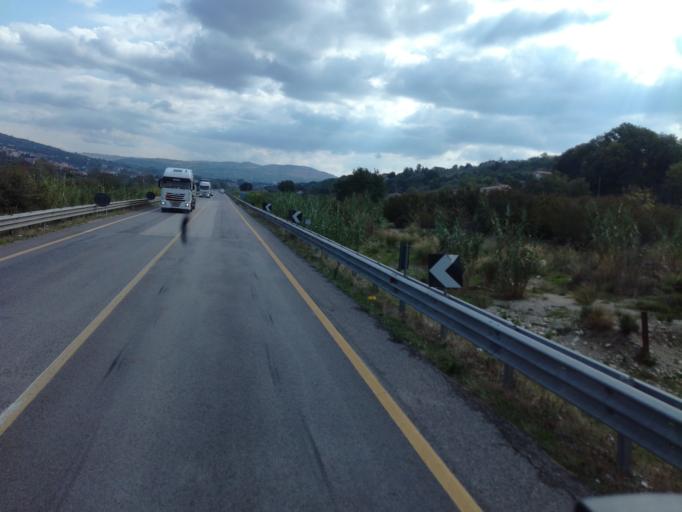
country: IT
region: Campania
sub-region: Provincia di Benevento
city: Paupisi
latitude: 41.2091
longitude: 14.6694
